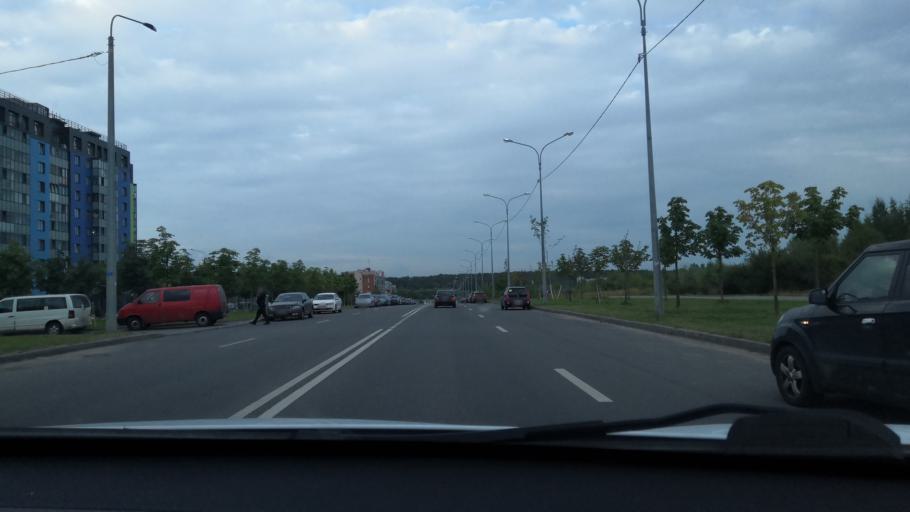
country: RU
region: St.-Petersburg
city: Pavlovsk
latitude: 59.6950
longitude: 30.4163
